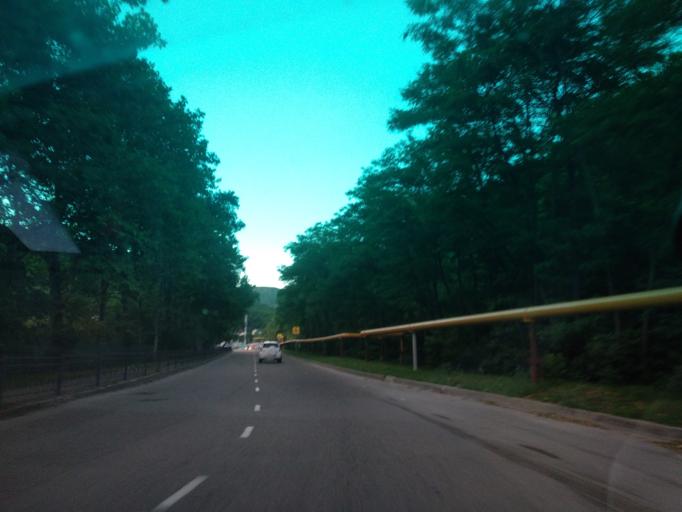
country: RU
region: Krasnodarskiy
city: Tuapse
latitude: 44.1181
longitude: 39.0690
